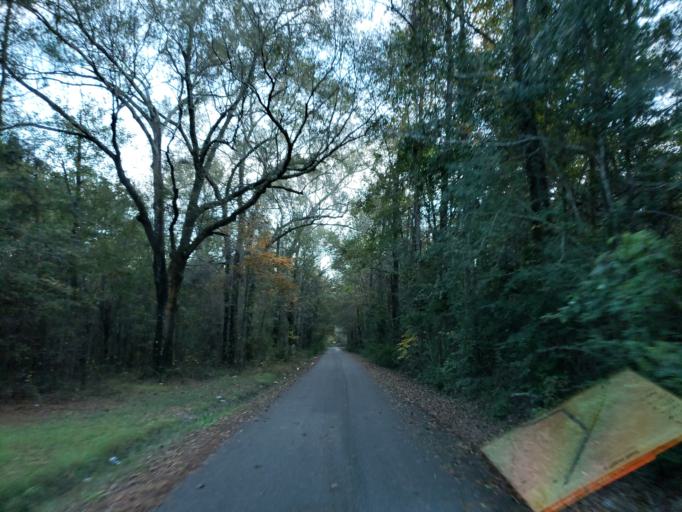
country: US
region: Mississippi
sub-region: Forrest County
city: Hattiesburg
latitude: 31.2832
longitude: -89.2544
